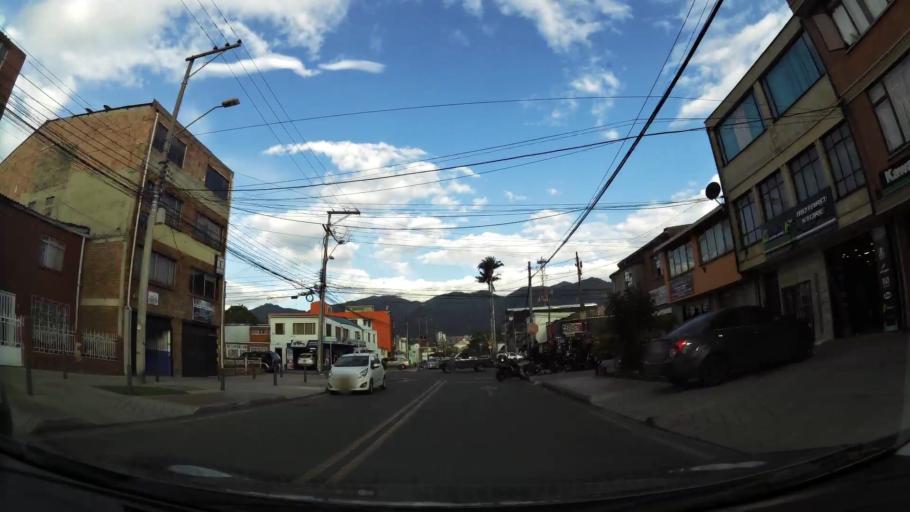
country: CO
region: Bogota D.C.
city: Bogota
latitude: 4.6533
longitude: -74.0746
